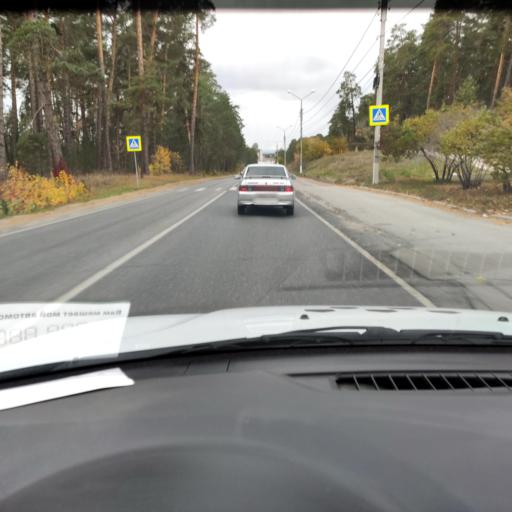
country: RU
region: Samara
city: Tol'yatti
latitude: 53.4758
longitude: 49.3391
